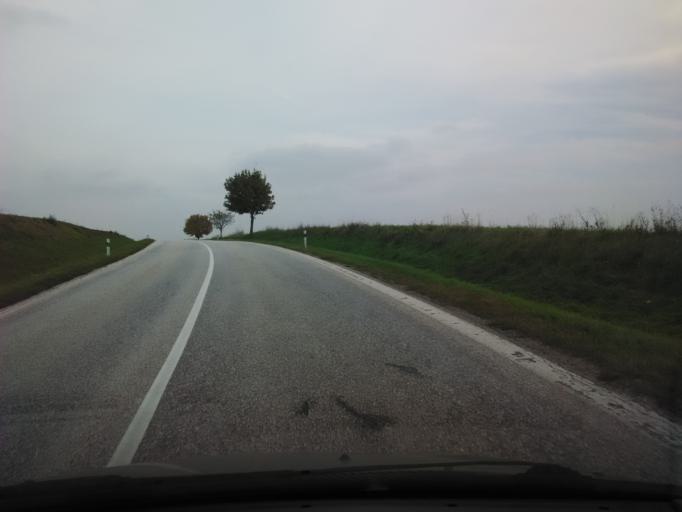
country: SK
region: Nitriansky
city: Svodin
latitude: 48.0131
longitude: 18.3954
